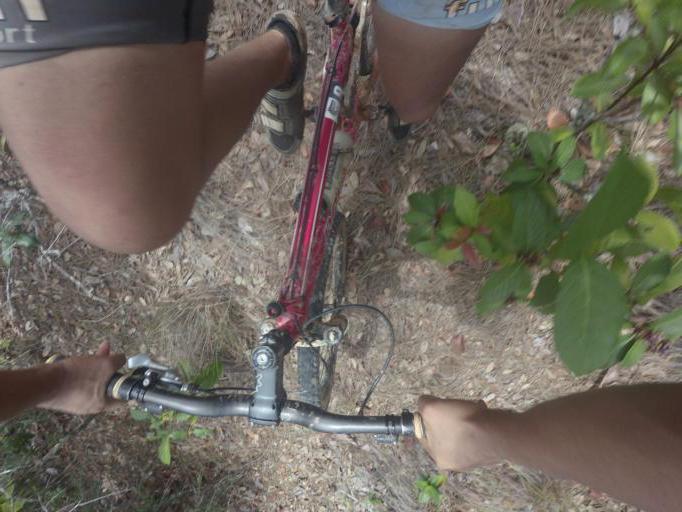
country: CU
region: Pinar del Rio
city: Vinales
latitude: 22.5810
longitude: -83.7718
